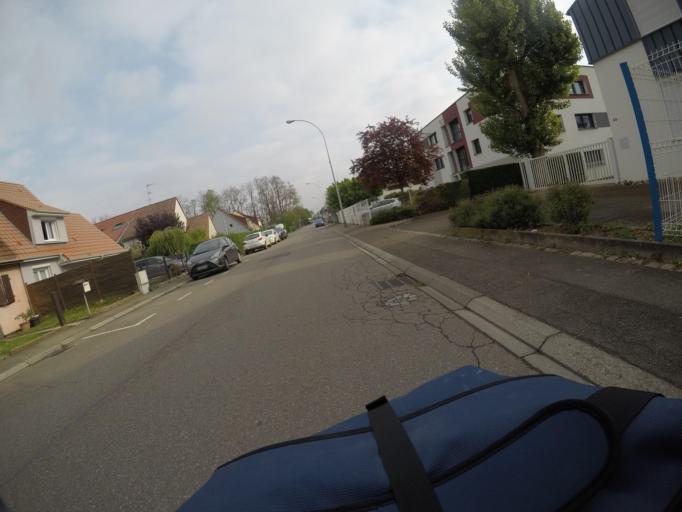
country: FR
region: Alsace
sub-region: Departement du Bas-Rhin
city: Wolfisheim
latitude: 48.5913
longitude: 7.6662
